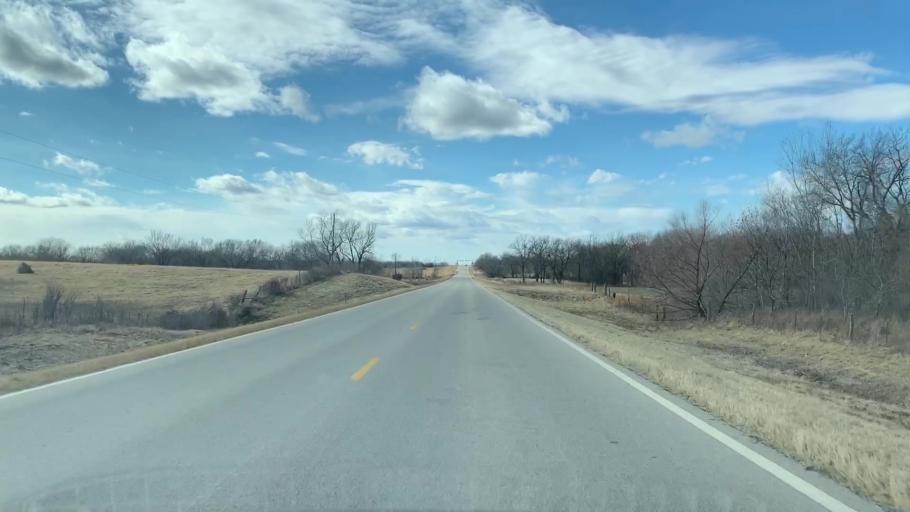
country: US
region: Kansas
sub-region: Neosho County
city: Chanute
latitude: 37.5288
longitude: -95.4587
